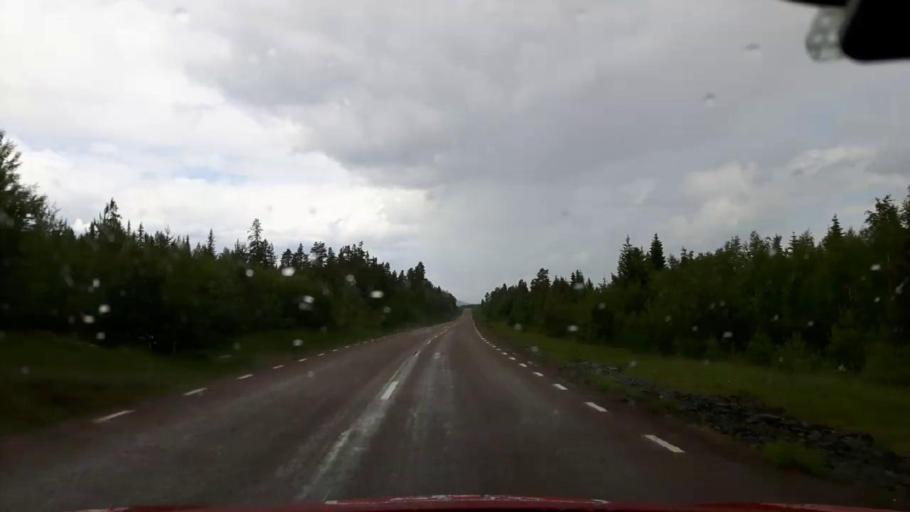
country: SE
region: Jaemtland
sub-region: Krokoms Kommun
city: Krokom
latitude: 63.8822
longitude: 14.2885
